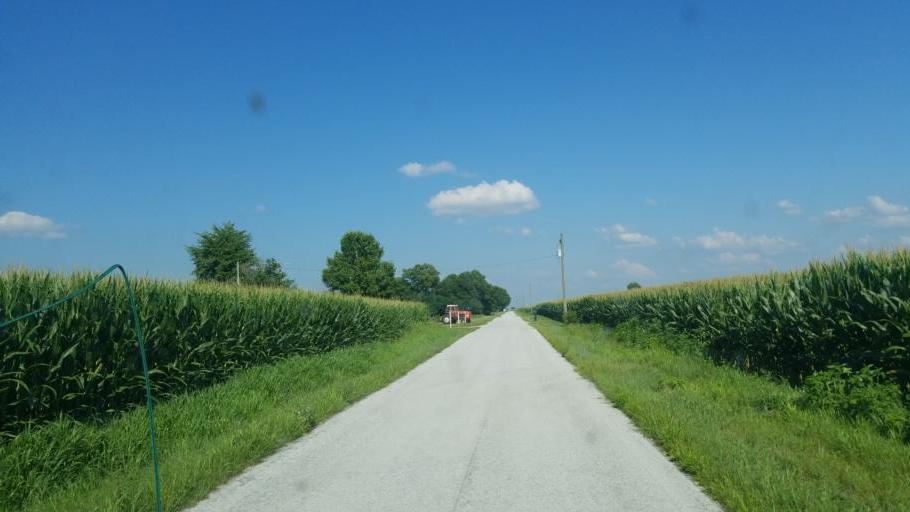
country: US
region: Ohio
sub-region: Hardin County
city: Kenton
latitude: 40.6873
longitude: -83.5223
